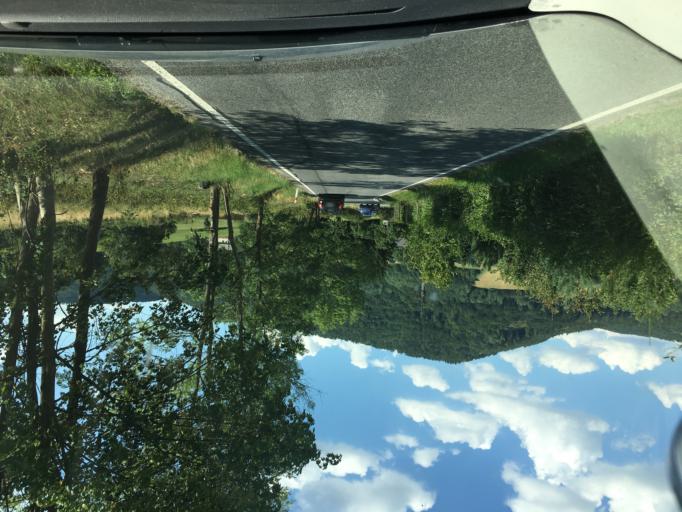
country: CZ
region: Liberecky
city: Mala Skala
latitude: 50.6401
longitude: 15.1837
